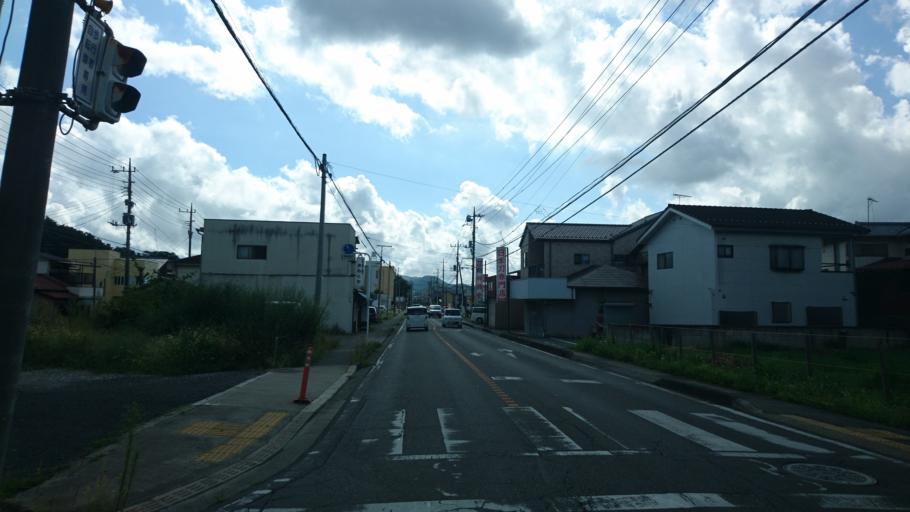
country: JP
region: Gunma
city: Kiryu
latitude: 36.4151
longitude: 139.3250
